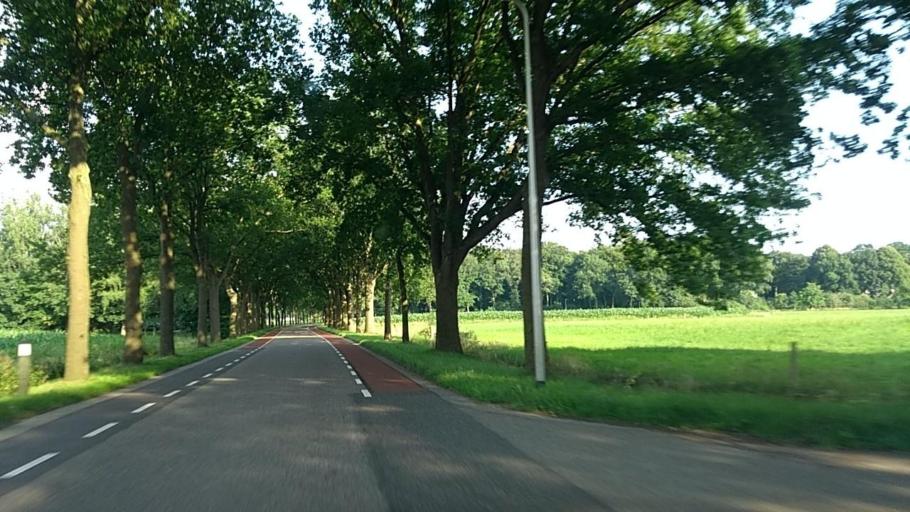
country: NL
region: Overijssel
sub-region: Gemeente Zwolle
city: Zwolle
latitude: 52.5442
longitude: 6.1364
